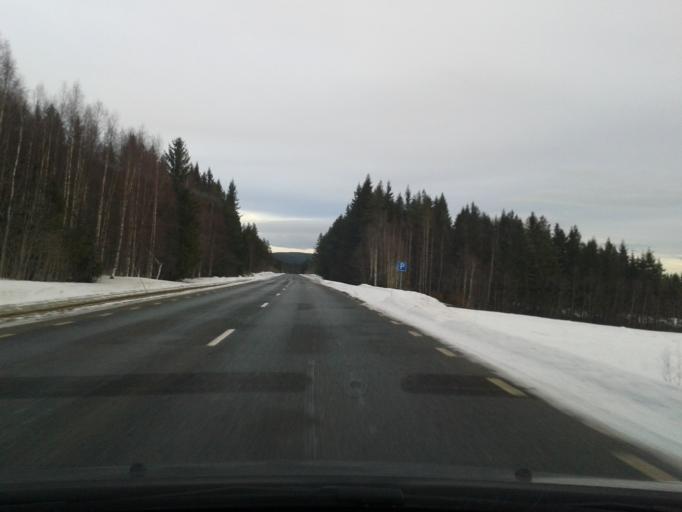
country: SE
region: Vaesternorrland
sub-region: Solleftea Kommun
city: As
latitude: 63.4419
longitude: 16.9189
